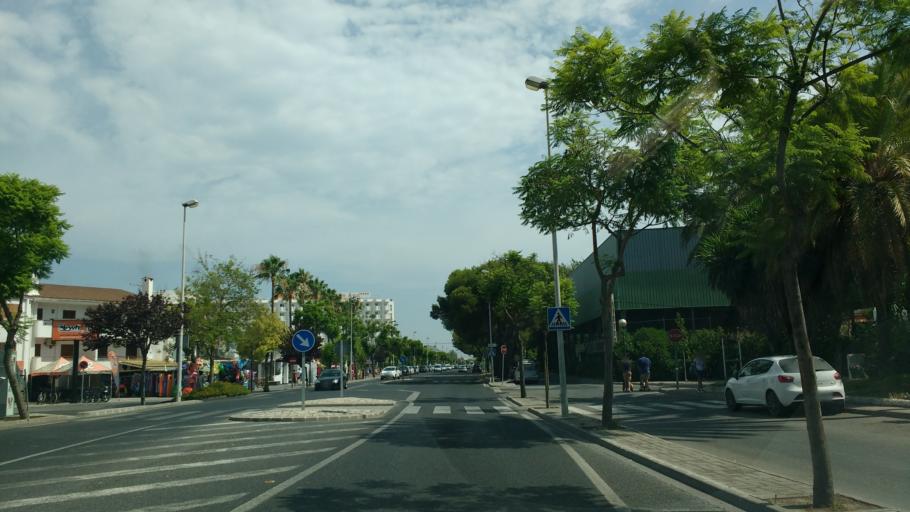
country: ES
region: Balearic Islands
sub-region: Illes Balears
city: Port d'Alcudia
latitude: 39.8349
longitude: 3.1182
